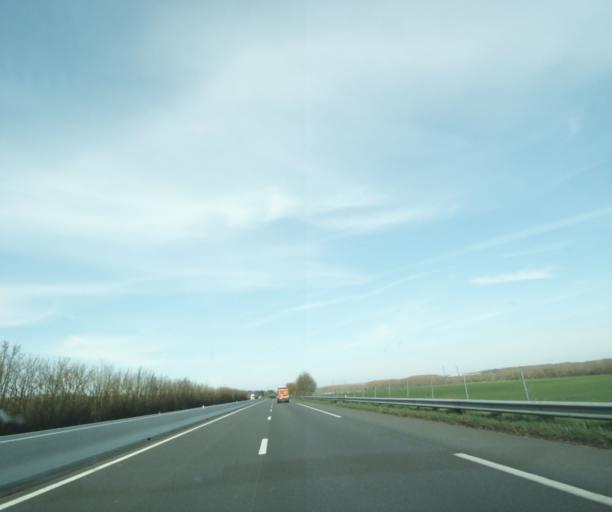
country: FR
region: Centre
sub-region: Departement du Cher
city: Massay
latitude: 47.1879
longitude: 2.0170
